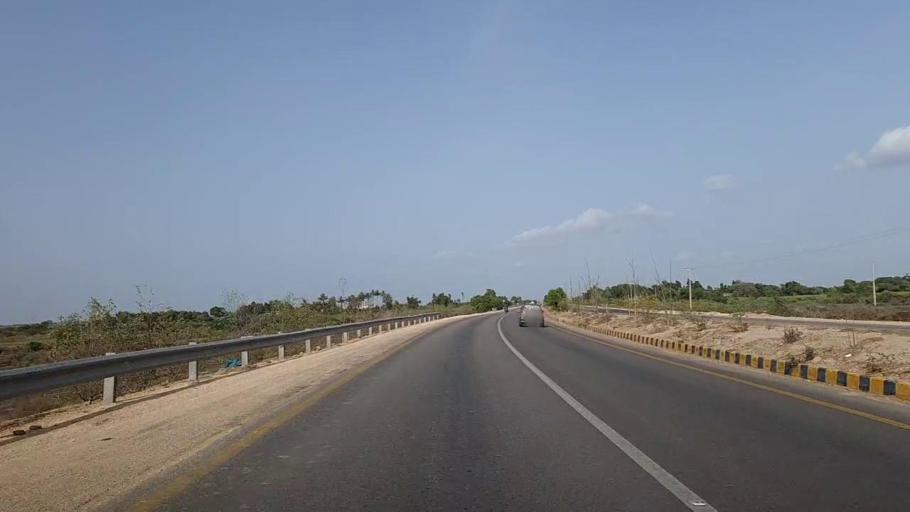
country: PK
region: Sindh
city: Gharo
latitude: 24.7357
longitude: 67.7018
